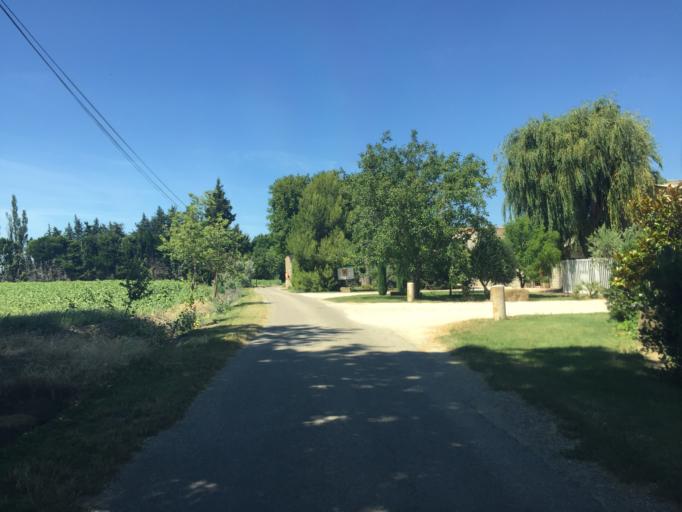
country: FR
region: Provence-Alpes-Cote d'Azur
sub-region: Departement du Vaucluse
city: Courthezon
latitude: 44.0719
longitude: 4.9158
